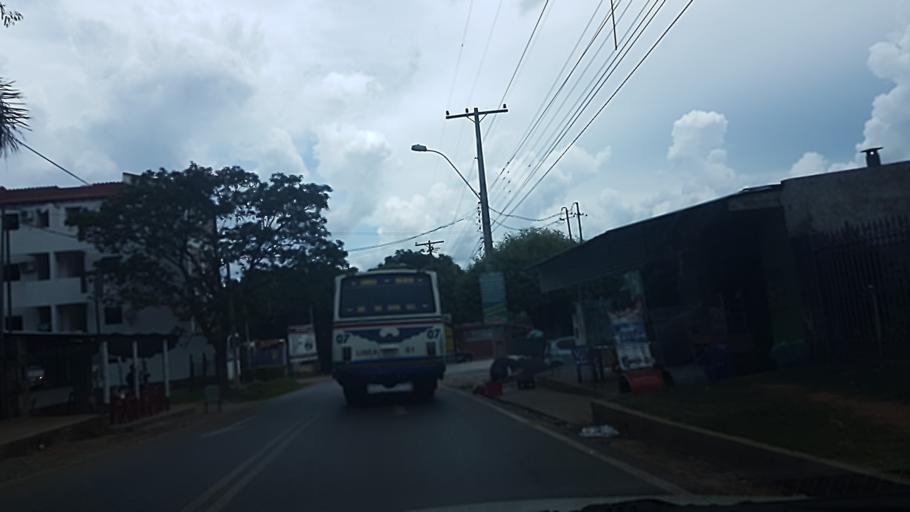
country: PY
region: Central
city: Limpio
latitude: -25.2097
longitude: -57.5145
